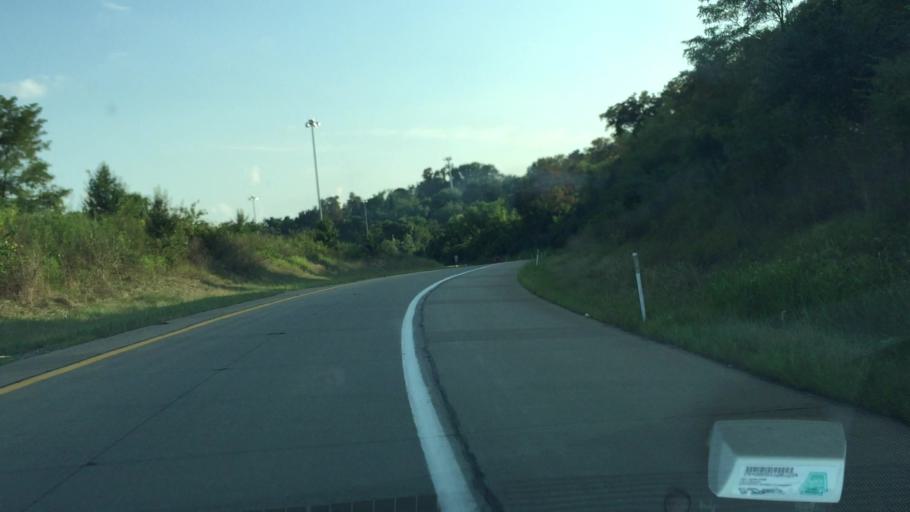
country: US
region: Pennsylvania
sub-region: Allegheny County
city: Ingram
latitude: 40.4532
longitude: -80.1119
